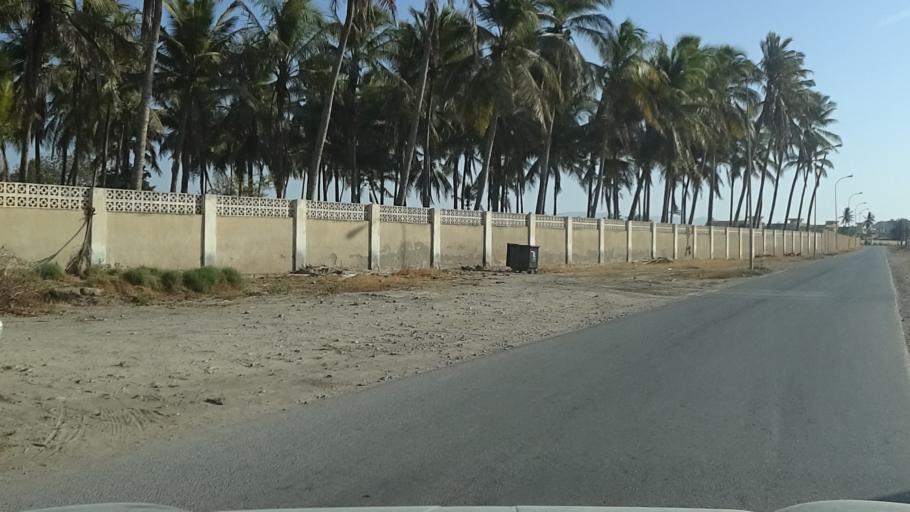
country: OM
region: Zufar
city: Salalah
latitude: 17.0195
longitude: 54.1491
